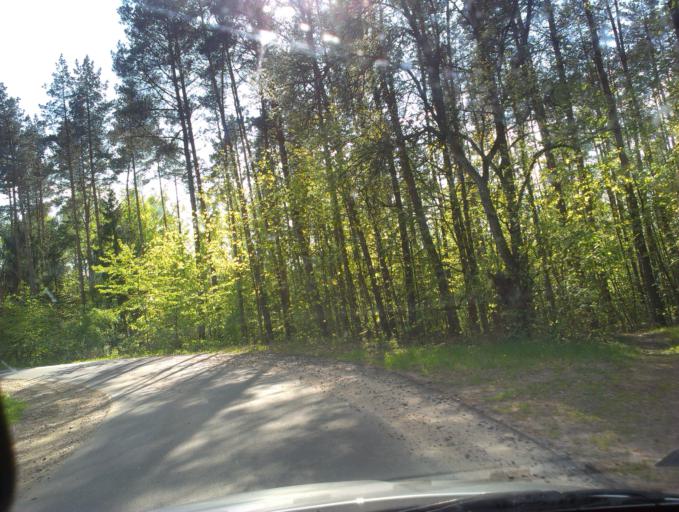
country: PL
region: West Pomeranian Voivodeship
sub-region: Powiat szczecinecki
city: Barwice
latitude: 53.7012
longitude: 16.2964
